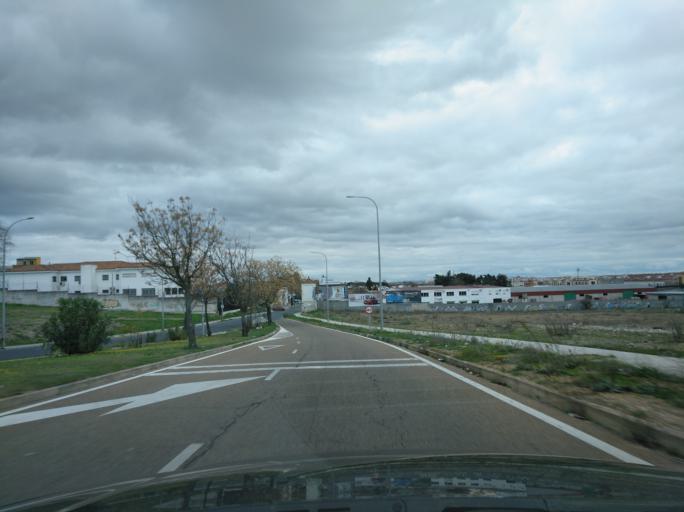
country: ES
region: Extremadura
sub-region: Provincia de Badajoz
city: Badajoz
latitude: 38.8949
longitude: -6.9834
